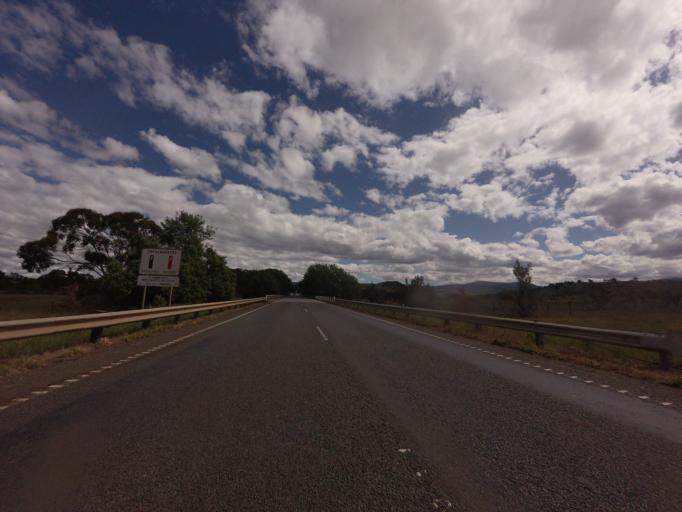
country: AU
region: Tasmania
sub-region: Northern Midlands
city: Evandale
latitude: -42.1370
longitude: 147.4228
